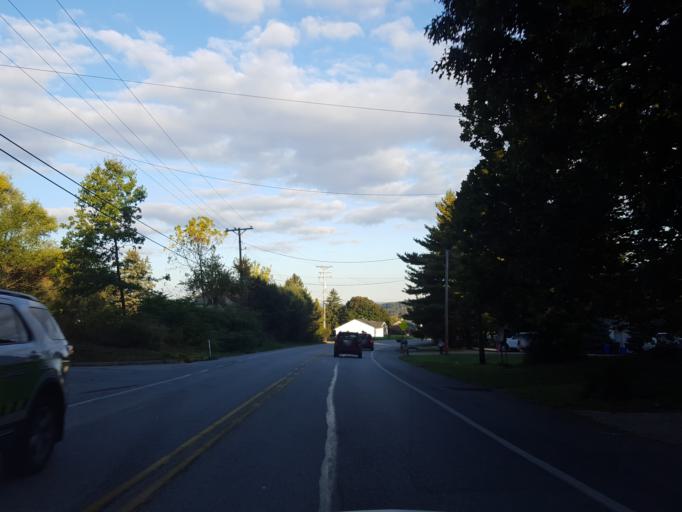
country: US
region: Pennsylvania
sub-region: York County
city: Yoe
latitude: 39.9310
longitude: -76.6415
